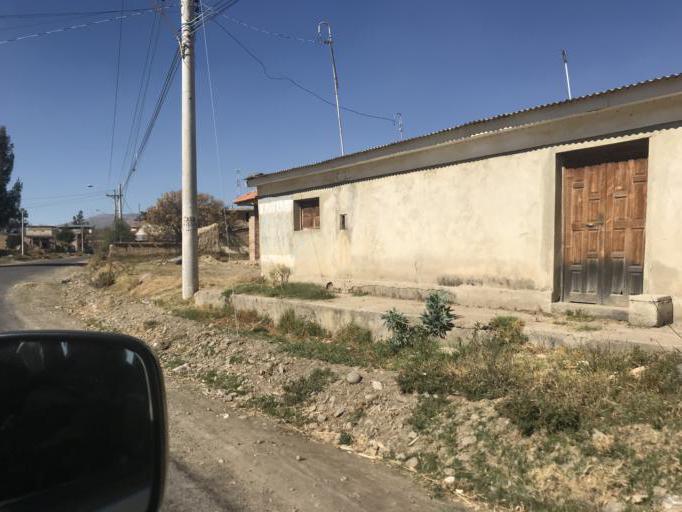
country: BO
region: Cochabamba
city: Cliza
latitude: -17.5666
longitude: -65.8911
